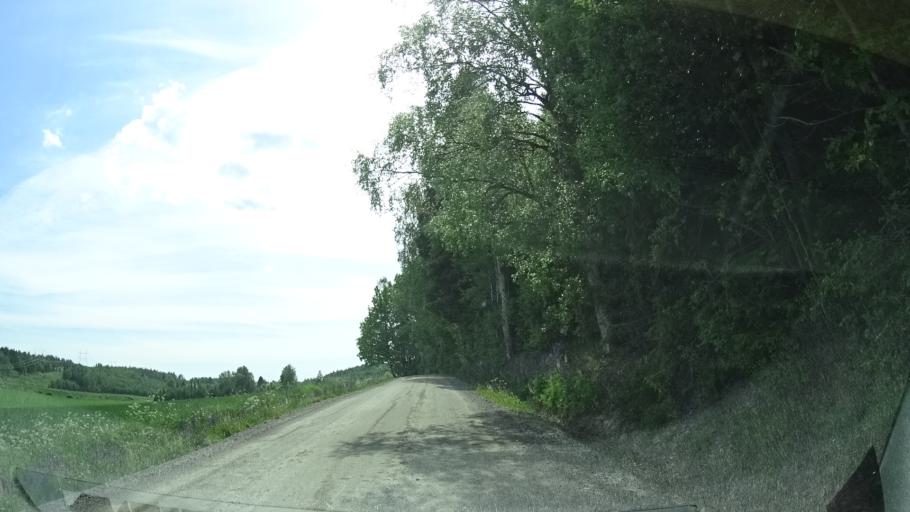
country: FI
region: Uusimaa
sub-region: Helsinki
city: Siuntio
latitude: 60.2003
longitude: 24.2557
